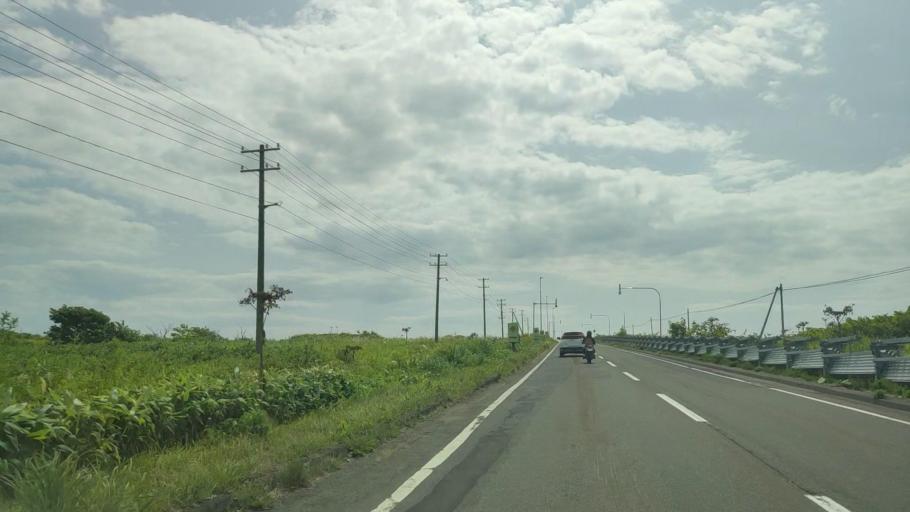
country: JP
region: Hokkaido
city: Rumoi
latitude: 44.4438
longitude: 141.7549
